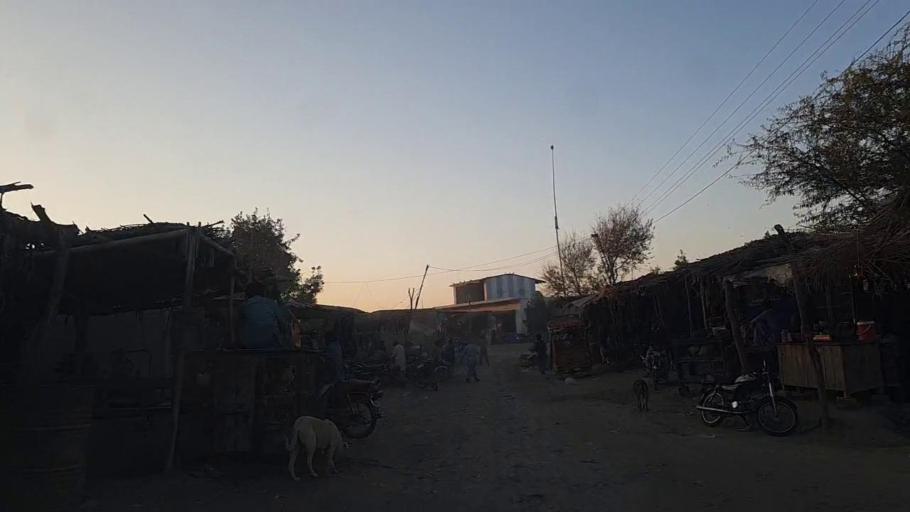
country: PK
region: Sindh
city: Naukot
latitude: 25.0577
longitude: 69.3989
